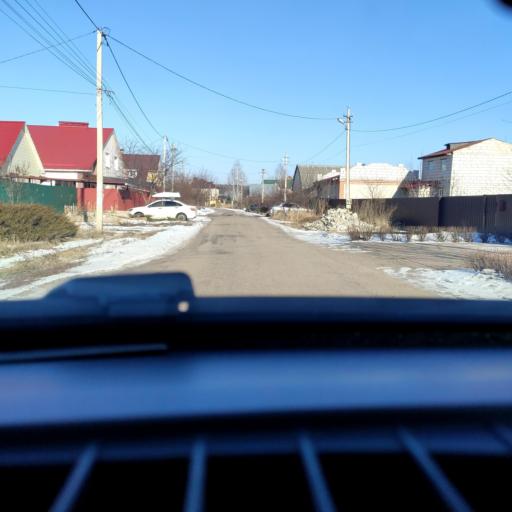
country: RU
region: Voronezj
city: Somovo
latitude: 51.6830
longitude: 39.3149
